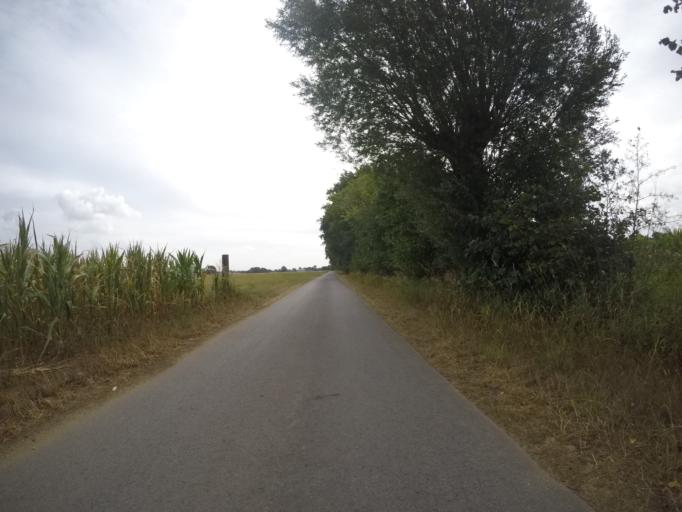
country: DE
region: North Rhine-Westphalia
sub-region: Regierungsbezirk Dusseldorf
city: Bocholt
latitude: 51.8583
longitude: 6.5526
